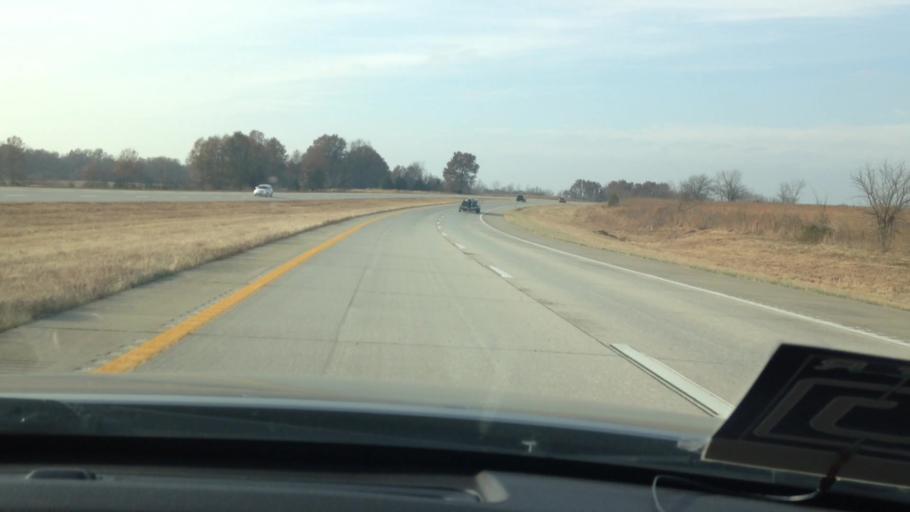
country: US
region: Missouri
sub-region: Henry County
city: Clinton
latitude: 38.4416
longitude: -93.9510
